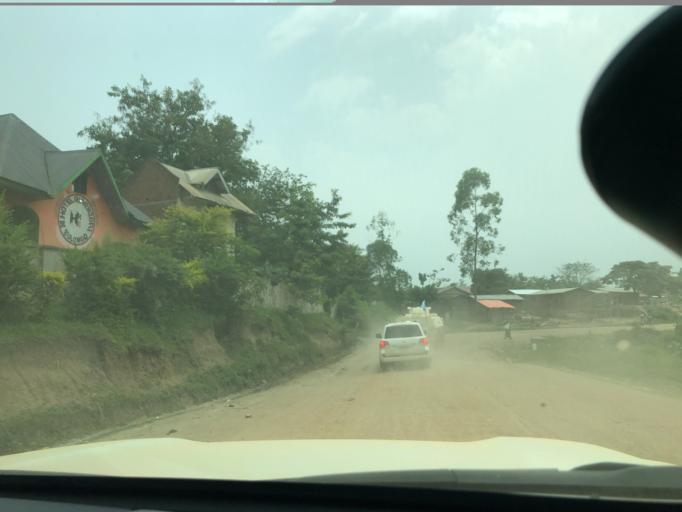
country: UG
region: Western Region
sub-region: Kasese District
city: Margherita
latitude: 0.3329
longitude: 29.6738
